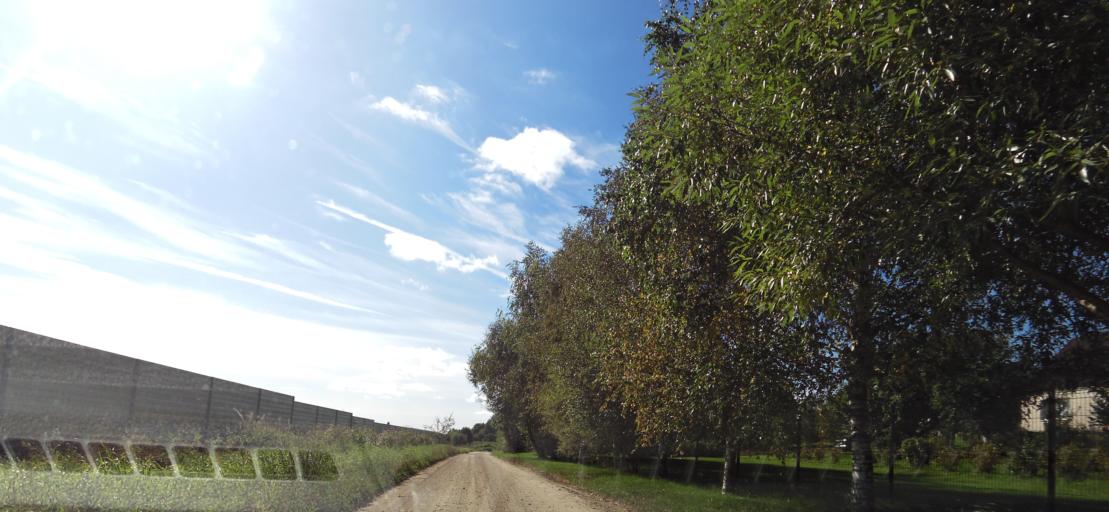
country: LT
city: Skaidiskes
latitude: 54.6370
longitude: 25.3617
